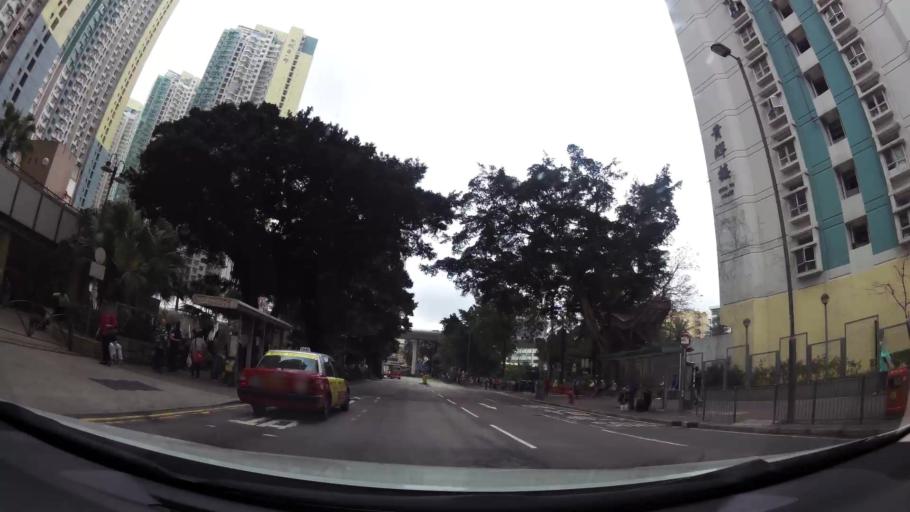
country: HK
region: Kowloon City
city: Kowloon
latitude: 22.3206
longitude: 114.2157
